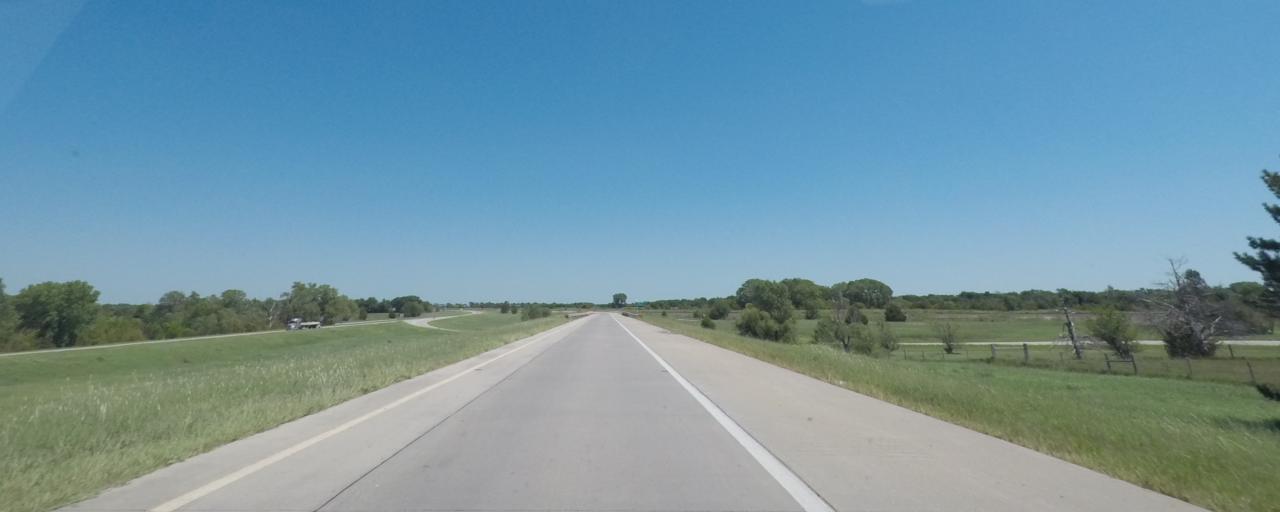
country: US
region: Kansas
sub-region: Harvey County
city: North Newton
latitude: 38.0663
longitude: -97.3155
